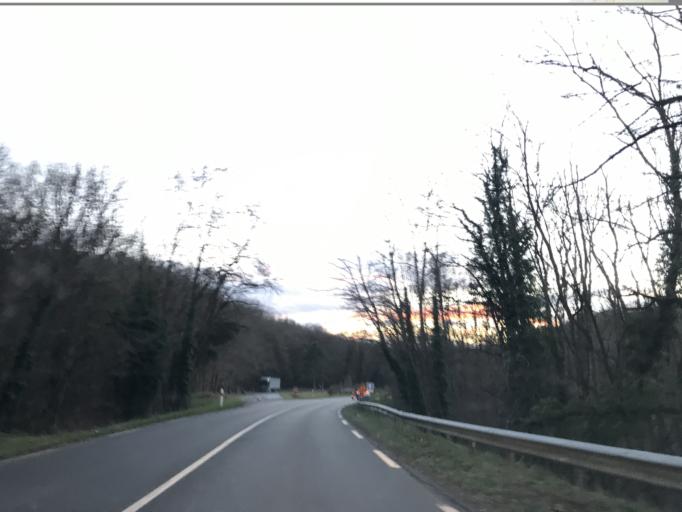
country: FR
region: Auvergne
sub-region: Departement du Puy-de-Dome
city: Peschadoires
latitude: 45.8306
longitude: 3.4585
